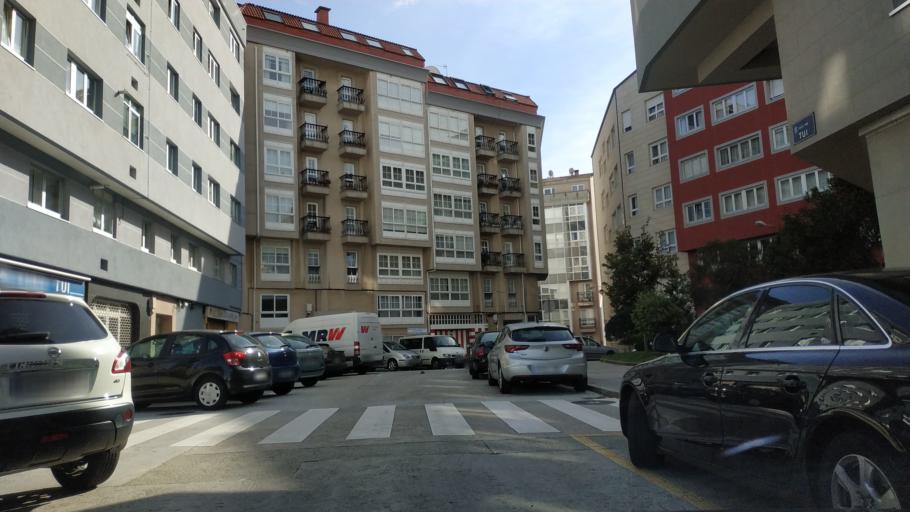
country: ES
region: Galicia
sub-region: Provincia da Coruna
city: A Coruna
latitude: 43.3755
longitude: -8.3961
